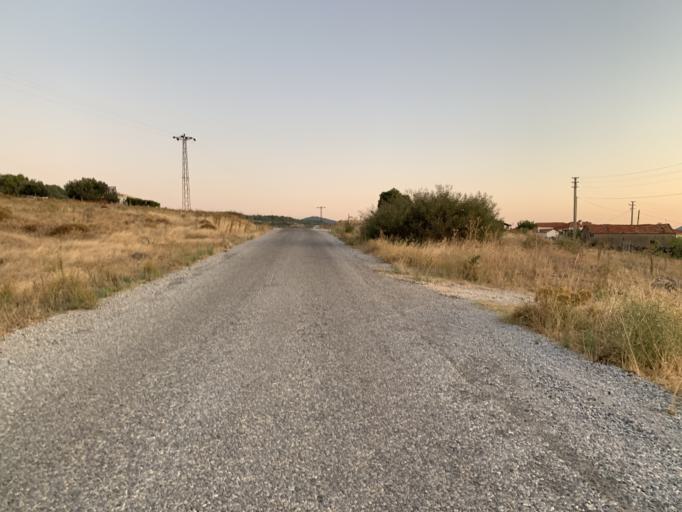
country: TR
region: Izmir
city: Uzunkuyu
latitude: 38.3249
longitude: 26.5835
